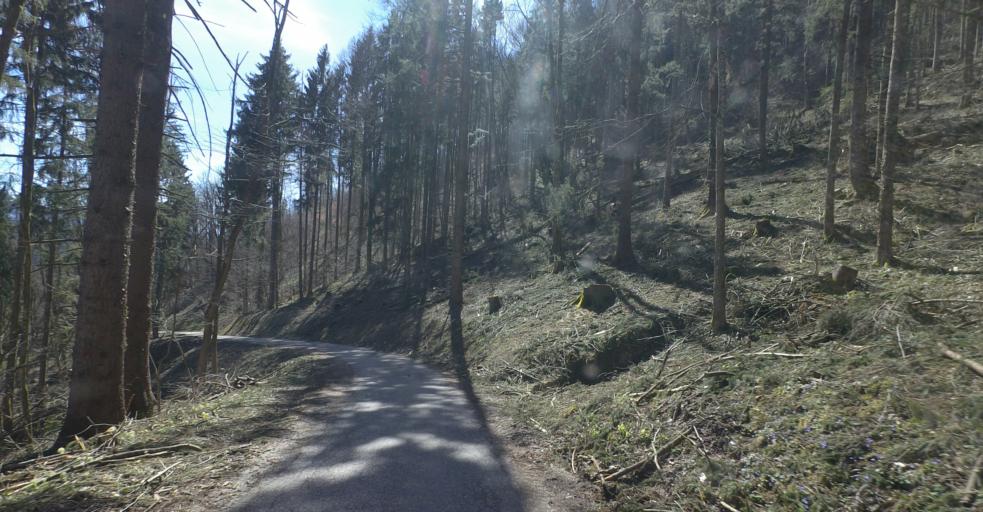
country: DE
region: Bavaria
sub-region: Upper Bavaria
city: Grassau
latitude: 47.7760
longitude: 12.4342
